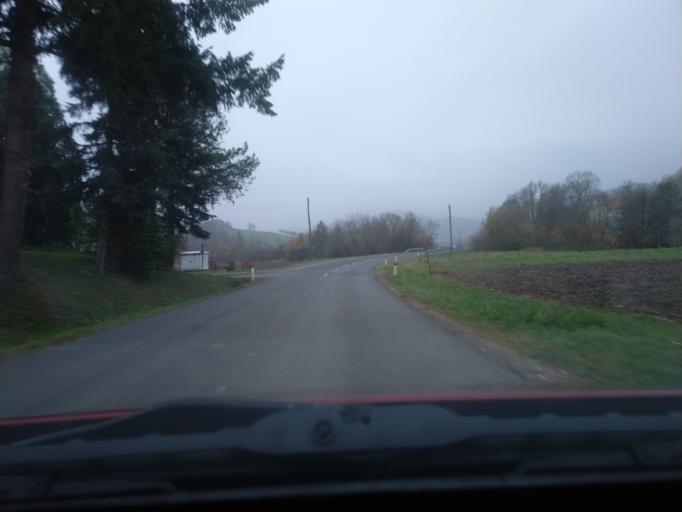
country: SI
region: Kungota
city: Zgornja Kungota
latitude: 46.6489
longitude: 15.6145
